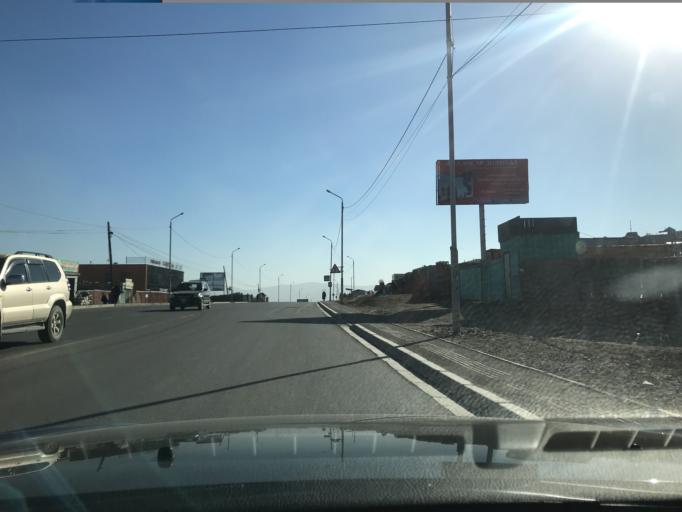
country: MN
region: Ulaanbaatar
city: Ulaanbaatar
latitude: 47.9944
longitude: 106.9257
